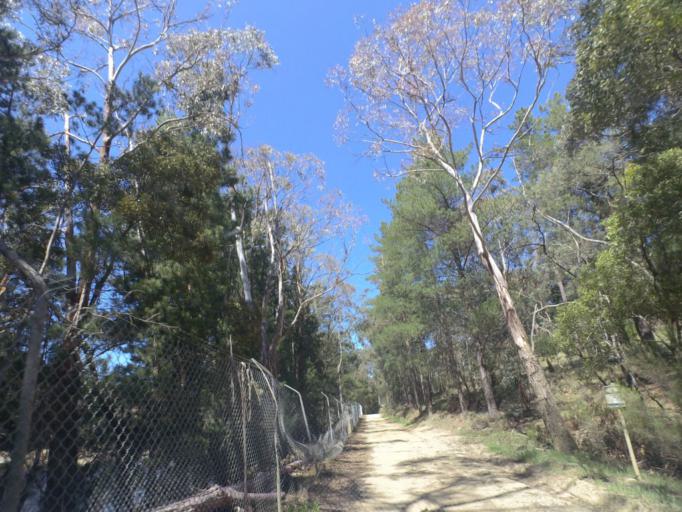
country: AU
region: Victoria
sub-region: Hume
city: Sunbury
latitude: -37.3956
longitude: 144.5570
